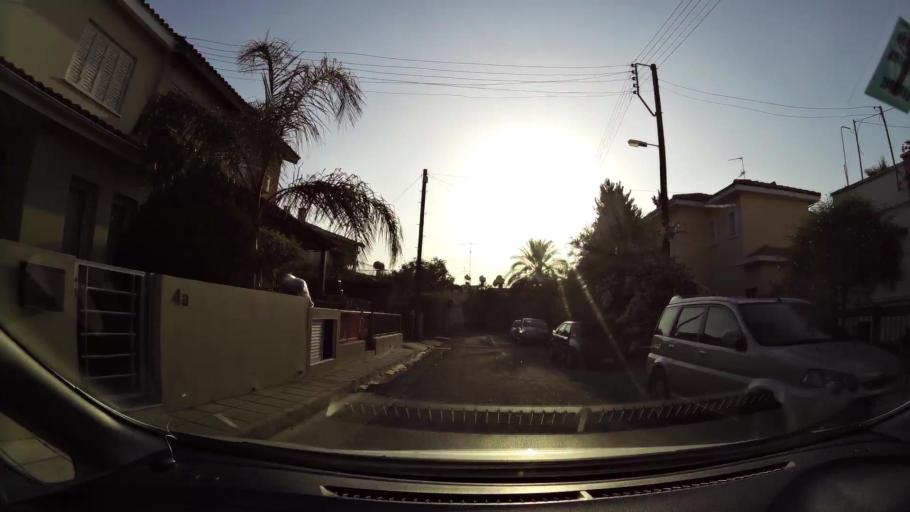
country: CY
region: Lefkosia
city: Nicosia
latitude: 35.1731
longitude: 33.3411
